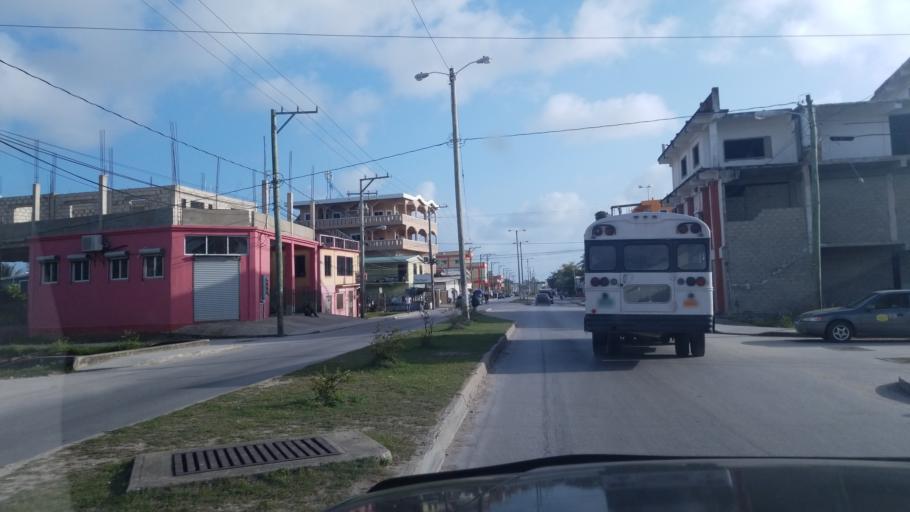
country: BZ
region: Belize
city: Belize City
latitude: 17.4917
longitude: -88.1989
